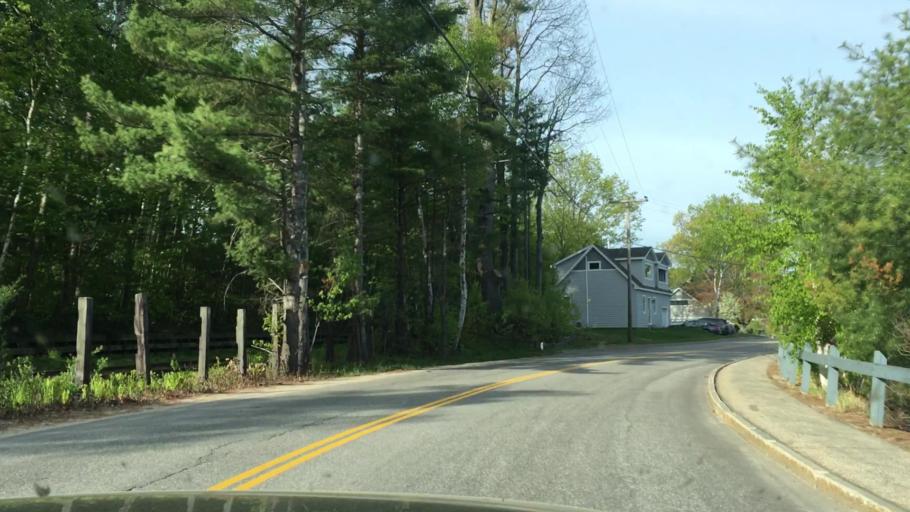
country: US
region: New Hampshire
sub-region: Belknap County
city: Meredith
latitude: 43.6482
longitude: -71.5058
